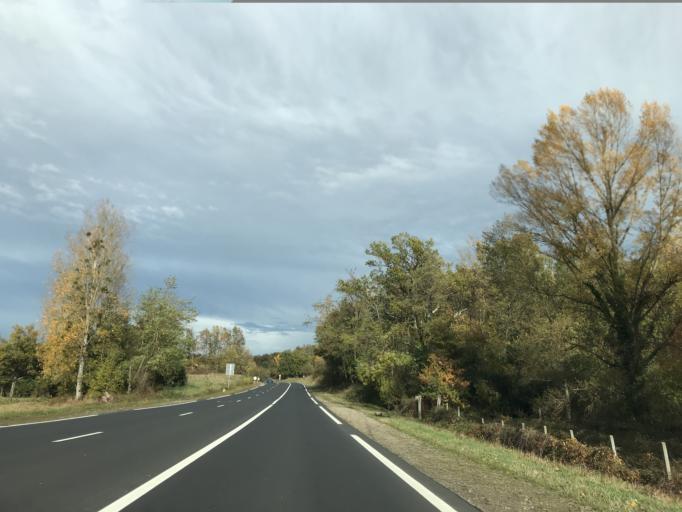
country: FR
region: Auvergne
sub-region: Departement du Puy-de-Dome
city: Peschadoires
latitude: 45.8497
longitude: 3.5074
